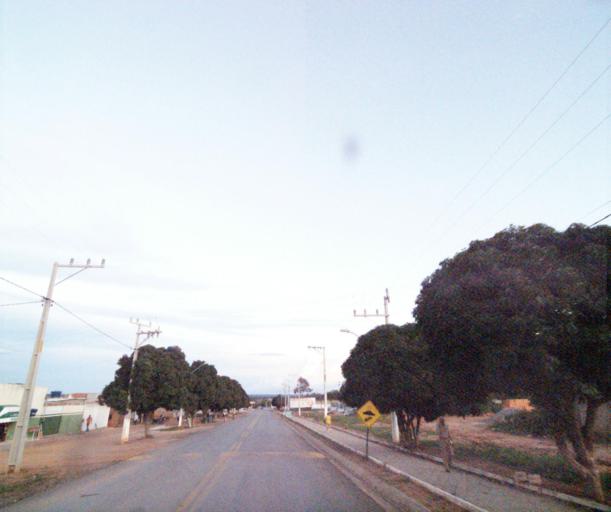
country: BR
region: Bahia
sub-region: Sao Felix Do Coribe
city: Santa Maria da Vitoria
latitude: -13.8246
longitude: -44.4640
